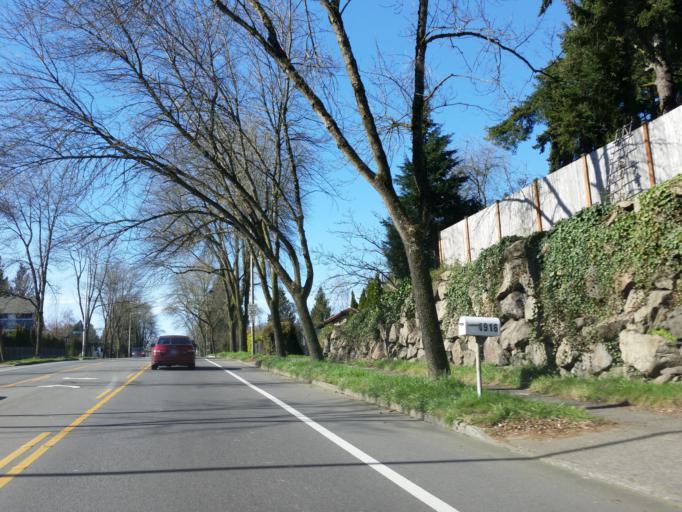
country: US
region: Washington
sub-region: King County
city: Lake Forest Park
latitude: 47.7194
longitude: -122.3078
